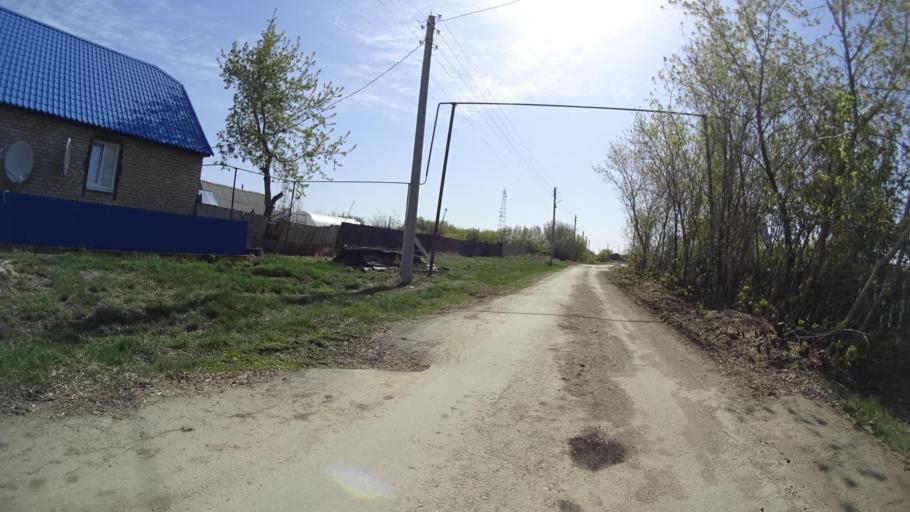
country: RU
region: Chelyabinsk
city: Chesma
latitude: 53.7928
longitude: 61.0344
